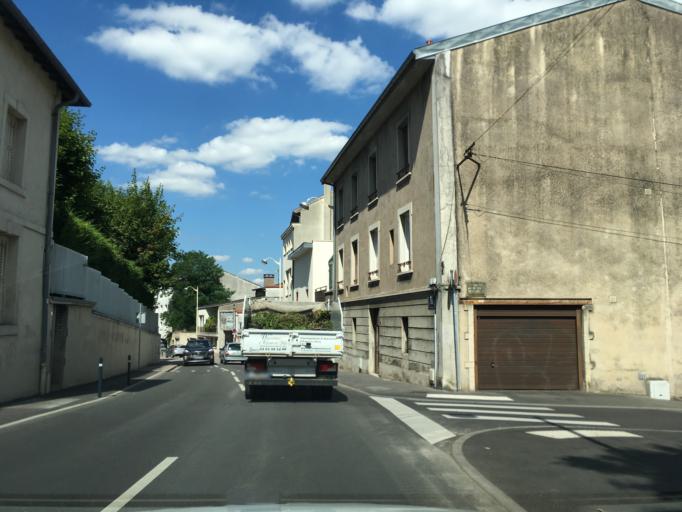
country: FR
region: Lorraine
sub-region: Departement de Meurthe-et-Moselle
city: Maxeville
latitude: 48.6920
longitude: 6.1635
